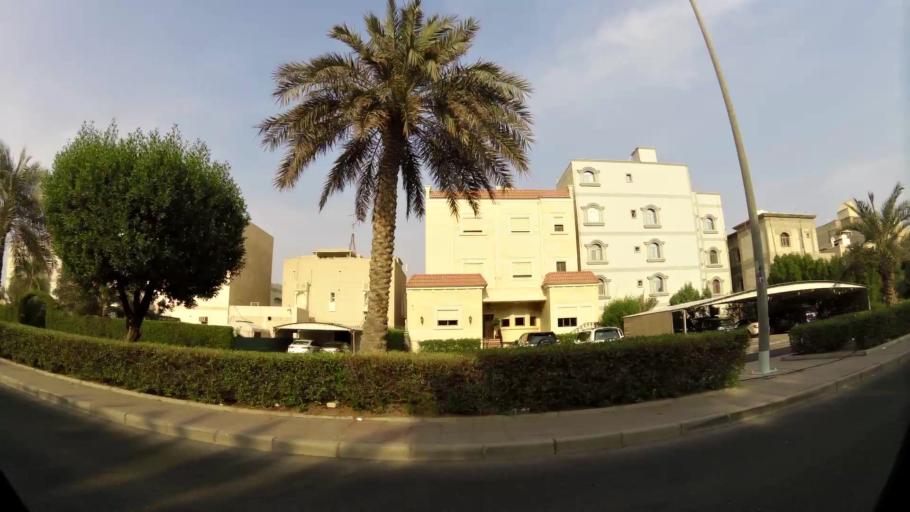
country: KW
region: Mubarak al Kabir
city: Mubarak al Kabir
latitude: 29.2152
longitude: 48.0642
